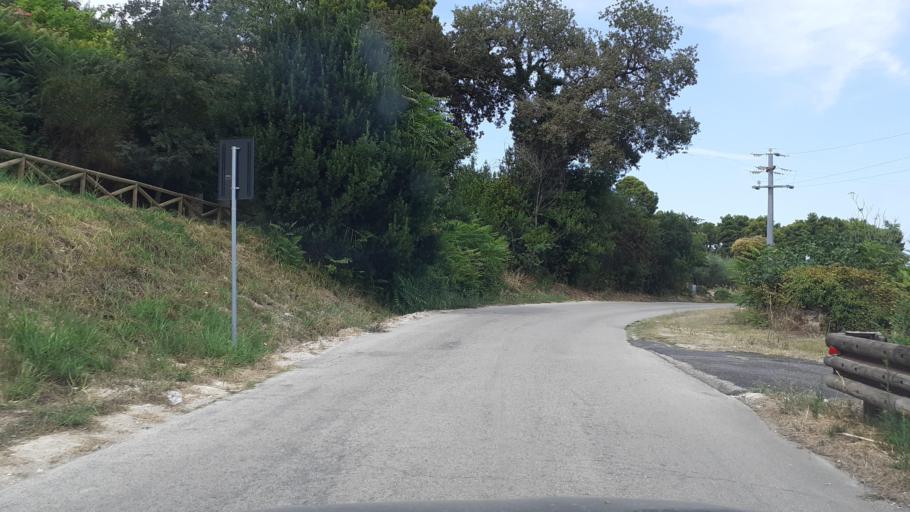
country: IT
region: Abruzzo
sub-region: Provincia di Chieti
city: Fossacesia
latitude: 42.2538
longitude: 14.4989
